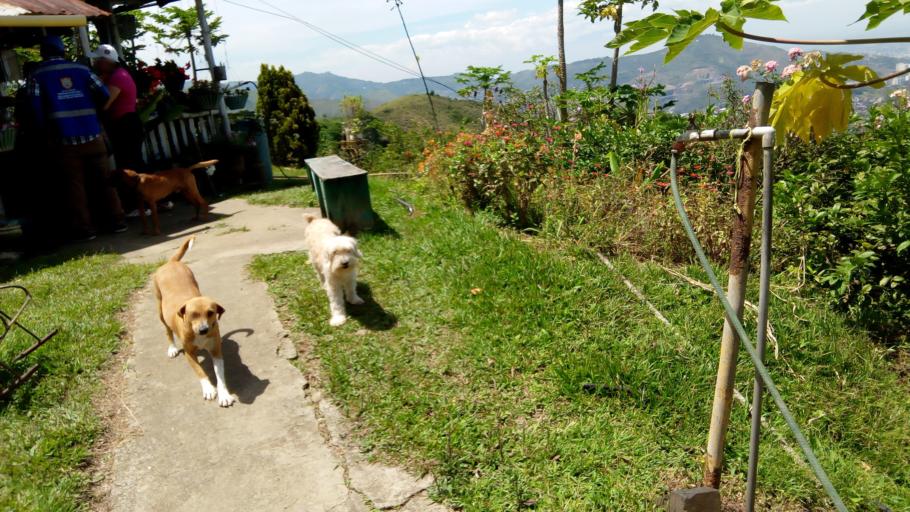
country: CO
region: Valle del Cauca
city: Cali
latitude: 3.4416
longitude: -76.5894
